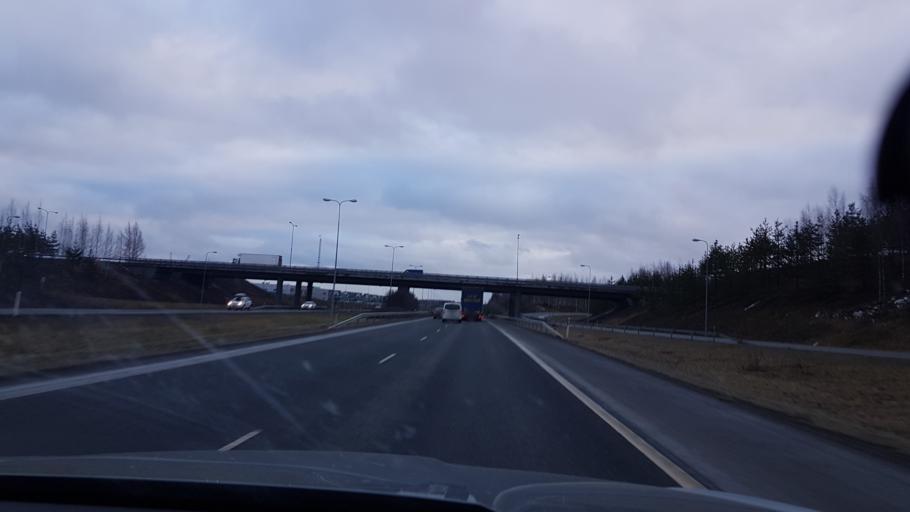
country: FI
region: Pirkanmaa
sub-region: Tampere
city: Lempaeaelae
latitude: 61.3673
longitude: 23.7902
